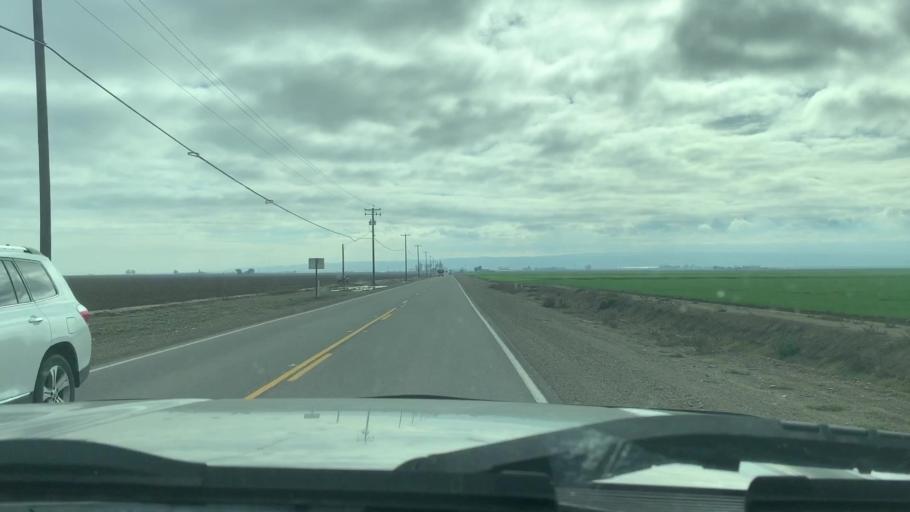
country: US
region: California
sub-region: Merced County
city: Los Banos
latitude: 37.0121
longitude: -120.8370
